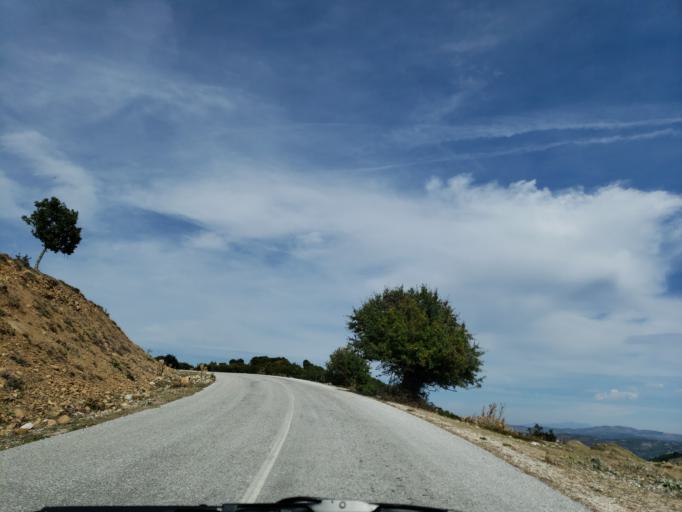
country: GR
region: Thessaly
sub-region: Trikala
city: Kastraki
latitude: 39.7629
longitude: 21.6644
